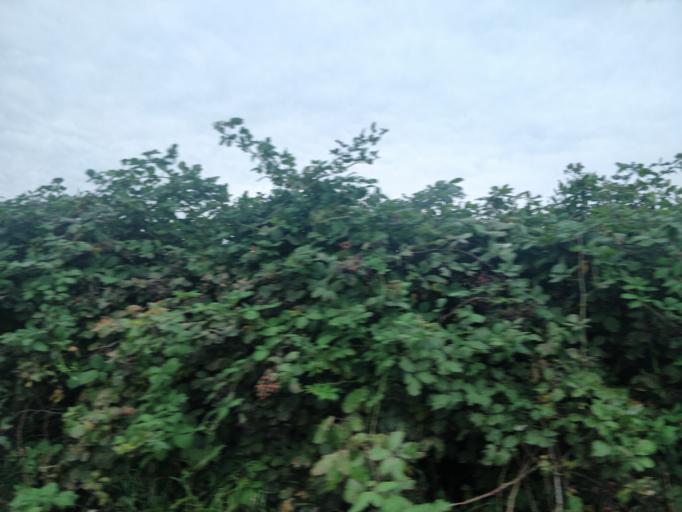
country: GB
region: England
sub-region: Lancashire
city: Ormskirk
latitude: 53.5946
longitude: -2.8630
